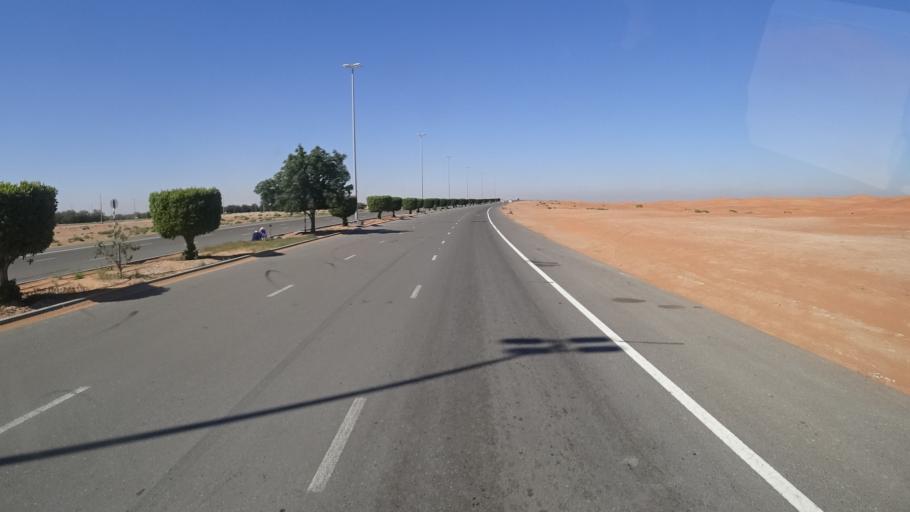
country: AE
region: Abu Dhabi
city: Al Ain
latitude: 24.0772
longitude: 55.6418
